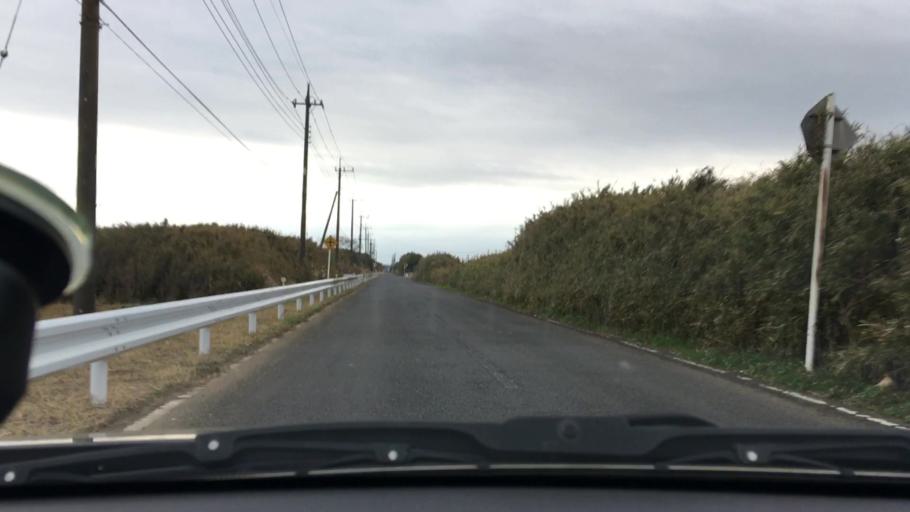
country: JP
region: Chiba
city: Omigawa
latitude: 35.8814
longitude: 140.6752
